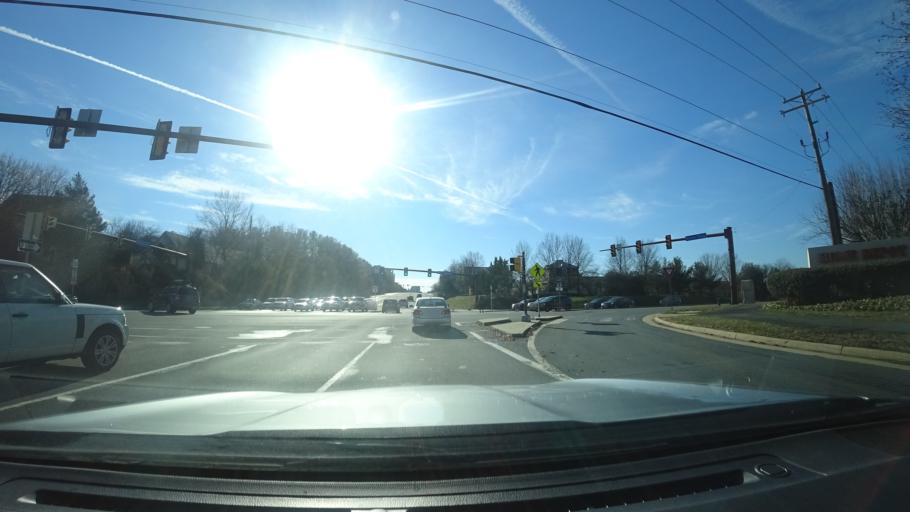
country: US
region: Virginia
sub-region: Fairfax County
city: Reston
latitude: 38.9674
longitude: -77.3539
